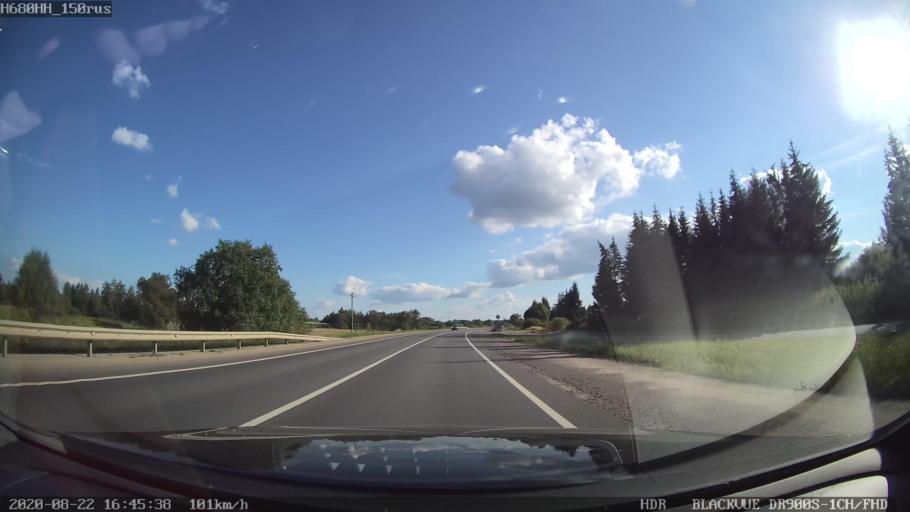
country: RU
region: Tverskaya
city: Rameshki
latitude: 57.2917
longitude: 36.0896
